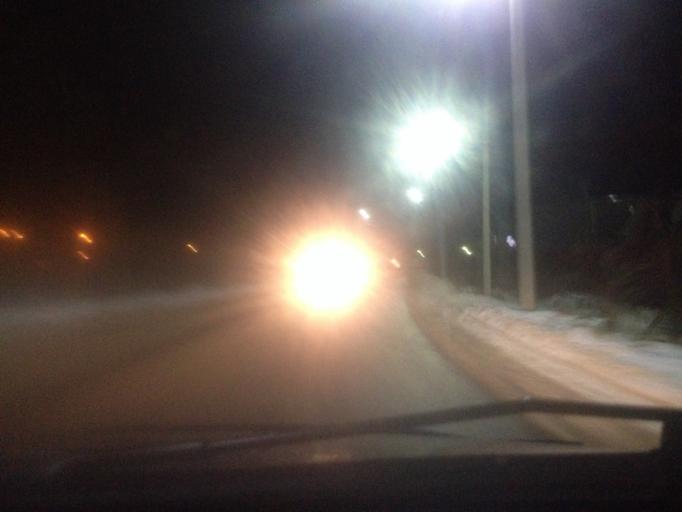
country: RU
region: Tula
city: Leninskiy
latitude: 54.2849
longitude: 37.4645
